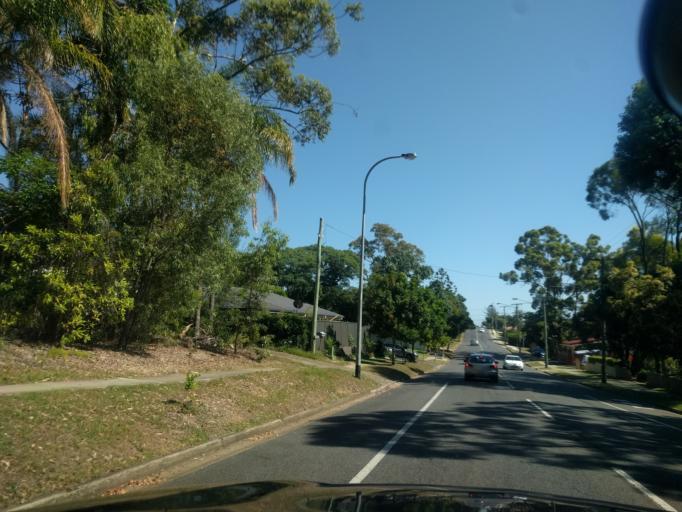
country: AU
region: Queensland
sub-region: Brisbane
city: Chermside West
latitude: -27.3740
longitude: 153.0145
